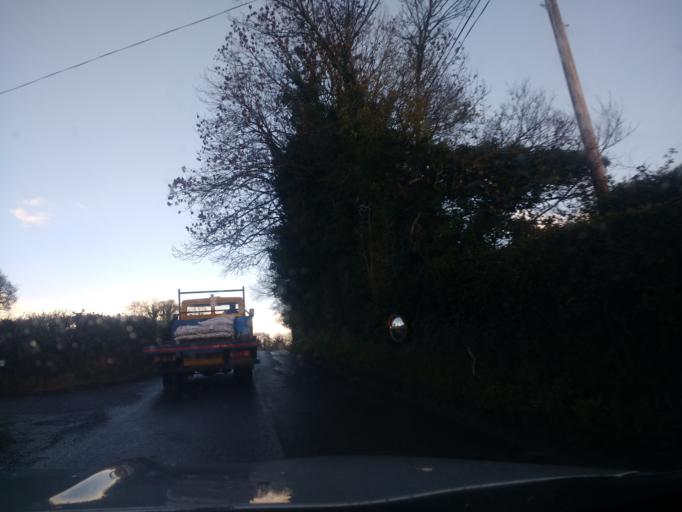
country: IE
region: Ulster
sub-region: County Donegal
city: Ramelton
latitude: 55.0551
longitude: -7.6368
